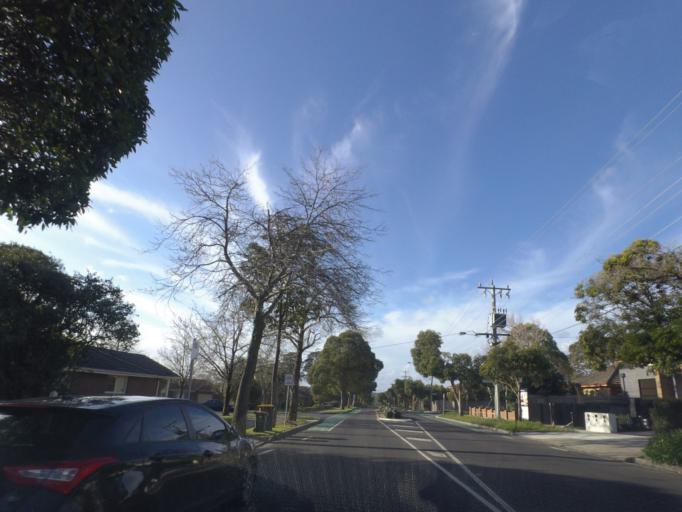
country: AU
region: Victoria
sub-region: Whitehorse
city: Box Hill
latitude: -37.8137
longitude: 145.1316
